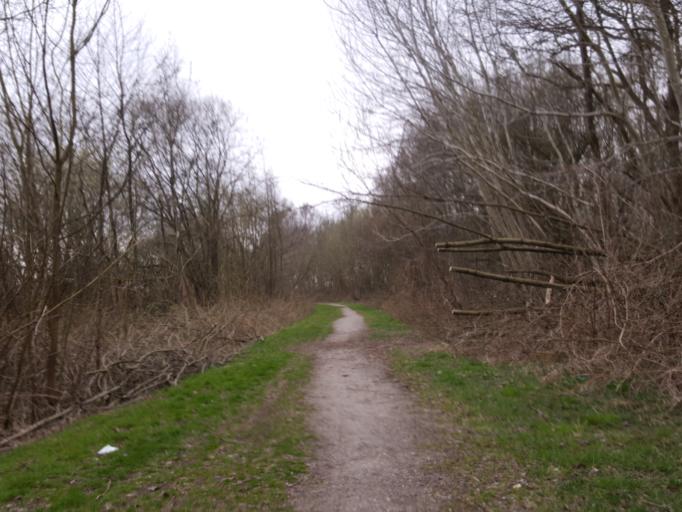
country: DE
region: Schleswig-Holstein
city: Oststeinbek
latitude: 53.5232
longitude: 10.1353
